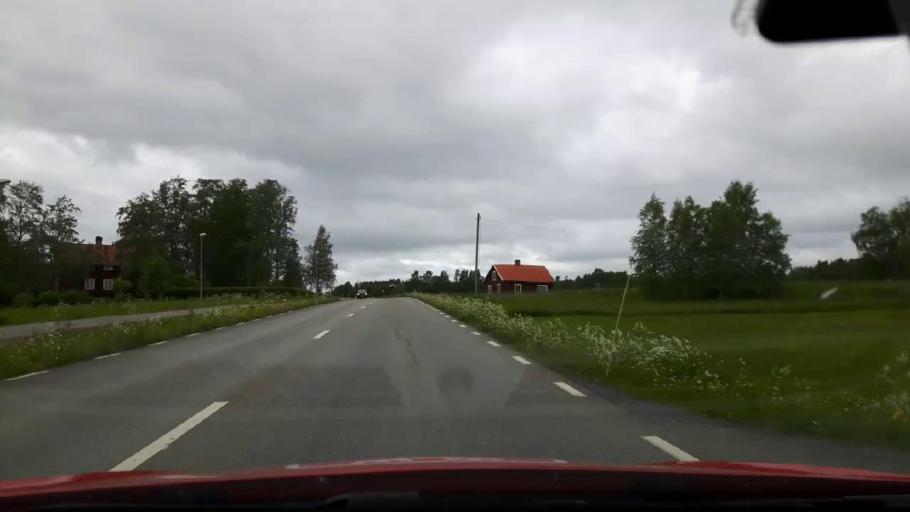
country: SE
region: Jaemtland
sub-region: OEstersunds Kommun
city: Ostersund
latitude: 63.2238
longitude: 14.5987
